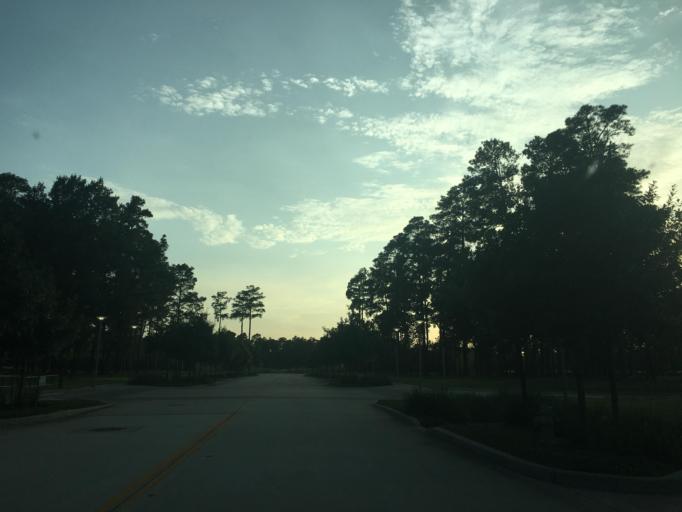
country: US
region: Texas
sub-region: Harris County
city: Spring
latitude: 30.0977
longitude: -95.4435
